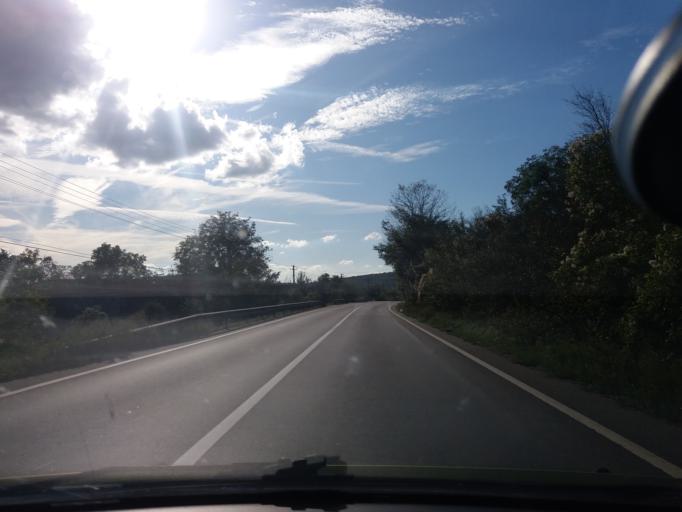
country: RO
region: Arad
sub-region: Comuna Conop
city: Conop
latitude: 46.1119
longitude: 21.8370
